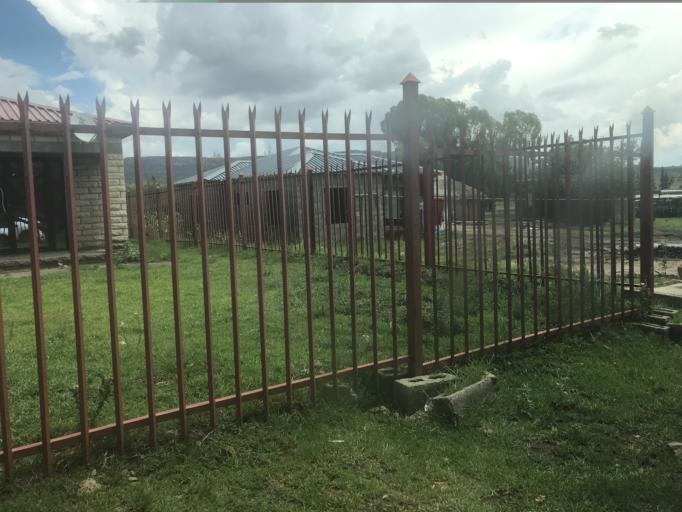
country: LS
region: Maseru
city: Nako
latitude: -29.6197
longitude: 27.5069
